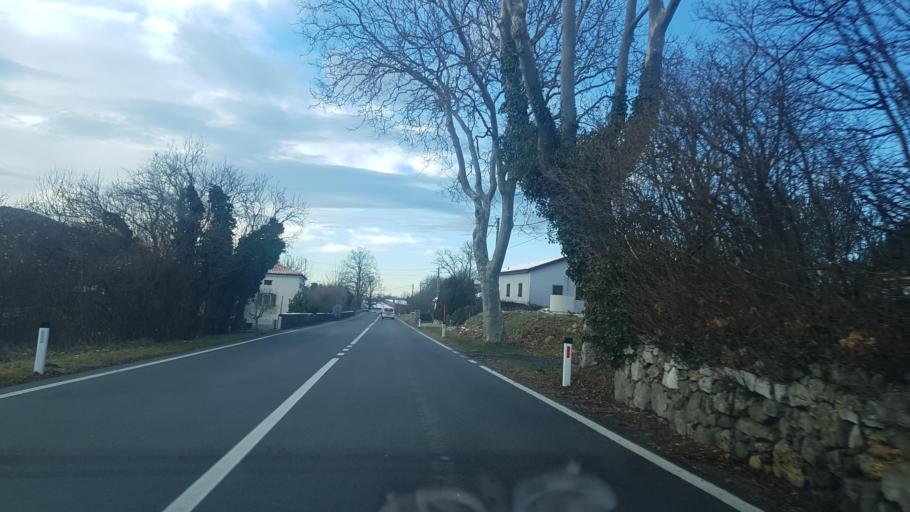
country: SI
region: Hrpelje-Kozina
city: Kozina
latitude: 45.5796
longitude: 13.9992
